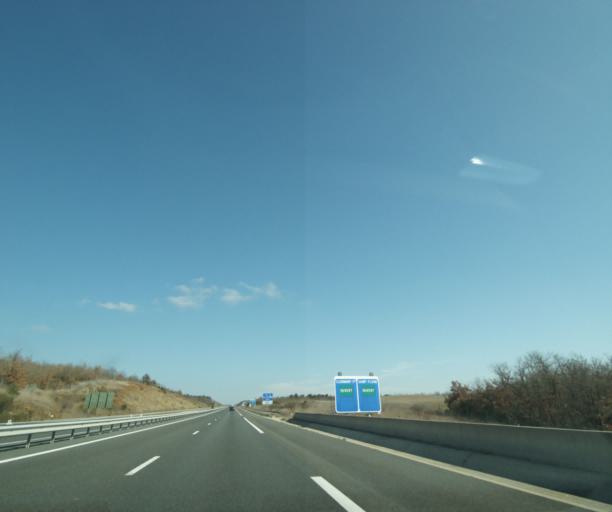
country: FR
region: Midi-Pyrenees
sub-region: Departement de l'Aveyron
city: Creissels
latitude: 44.1576
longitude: 3.0226
